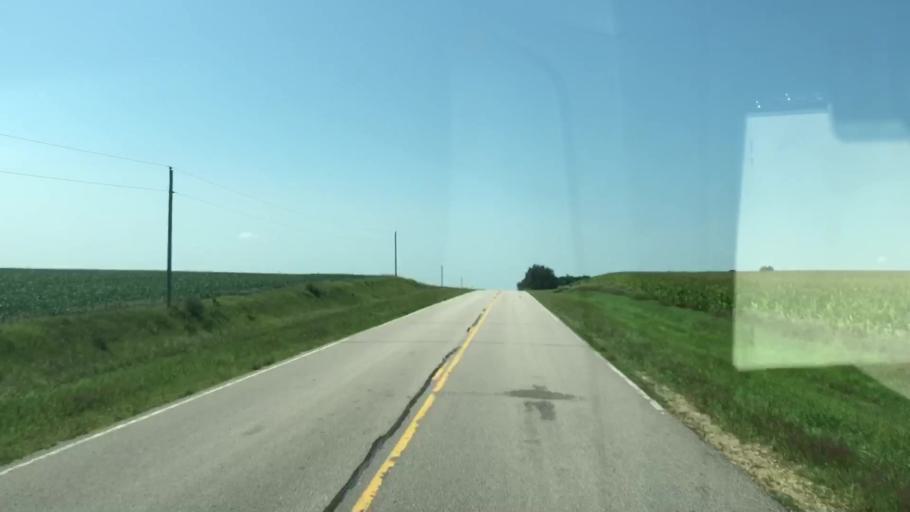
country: US
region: Iowa
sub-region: O'Brien County
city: Sanborn
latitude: 43.2443
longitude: -95.7337
